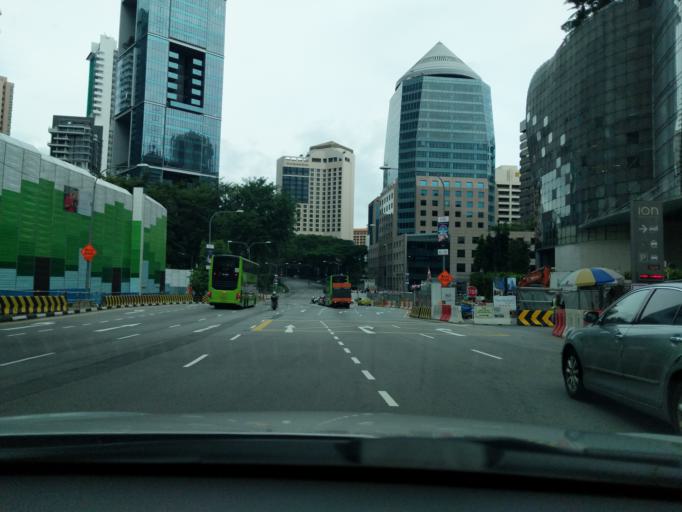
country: SG
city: Singapore
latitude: 1.3032
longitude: 103.8318
